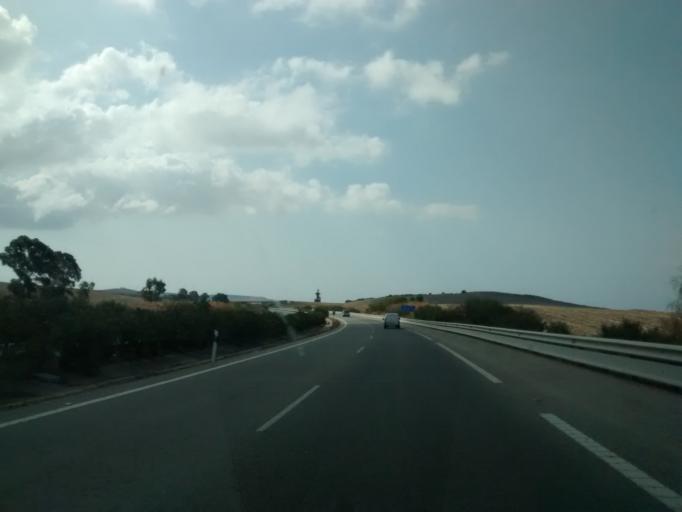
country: ES
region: Andalusia
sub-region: Provincia de Cadiz
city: Conil de la Frontera
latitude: 36.2633
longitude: -6.0299
